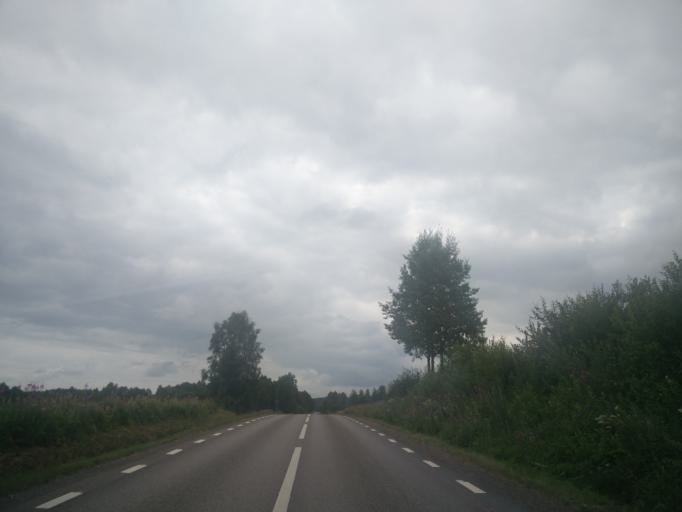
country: SE
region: Vaermland
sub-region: Torsby Kommun
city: Torsby
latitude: 59.9395
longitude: 12.9018
